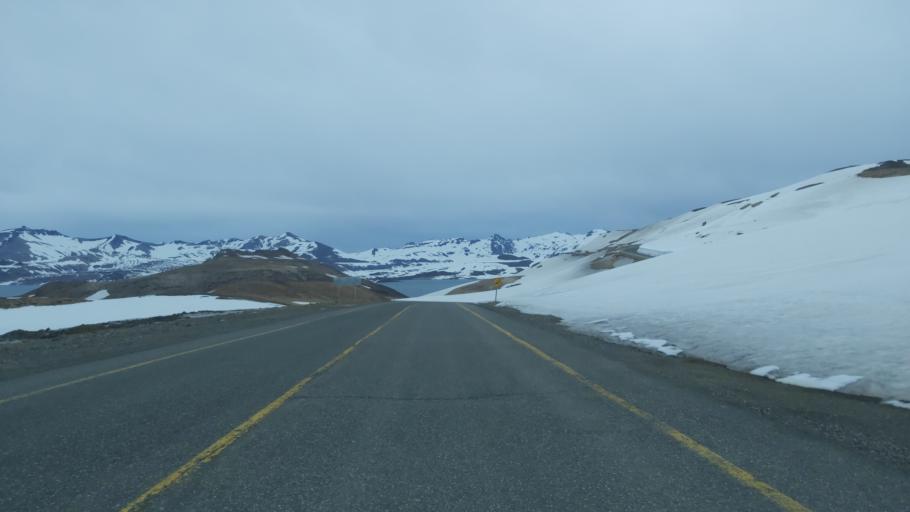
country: CL
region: Maule
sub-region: Provincia de Linares
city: Colbun
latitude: -36.0115
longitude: -70.4835
